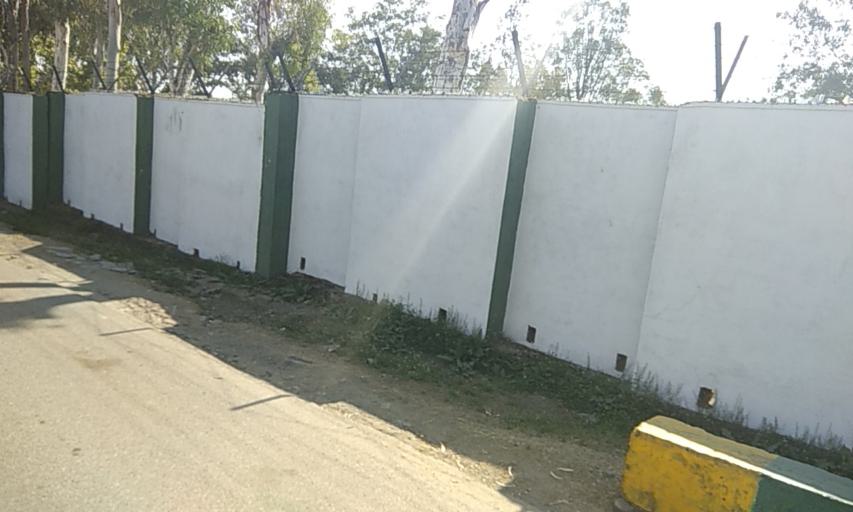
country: IN
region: Himachal Pradesh
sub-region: Kangra
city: Dharmsala
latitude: 32.1762
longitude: 76.3812
